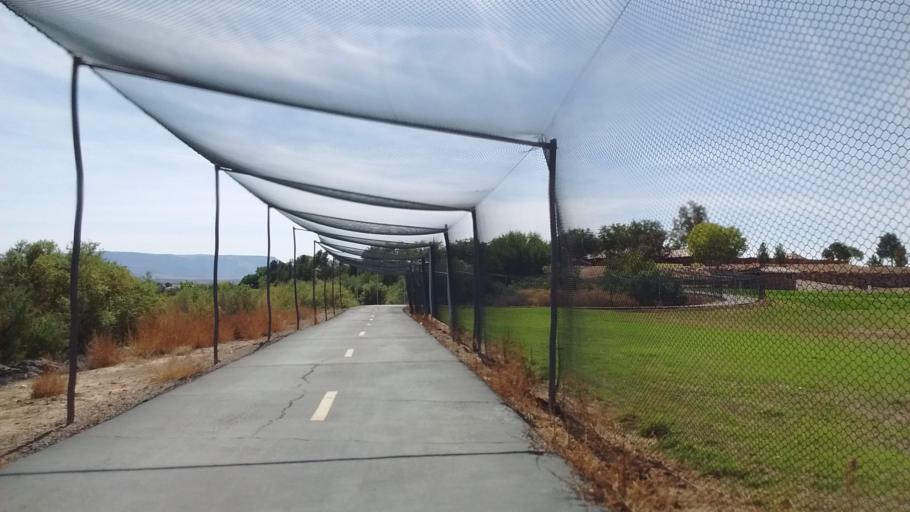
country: US
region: Utah
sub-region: Washington County
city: Saint George
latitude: 37.0562
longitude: -113.6009
